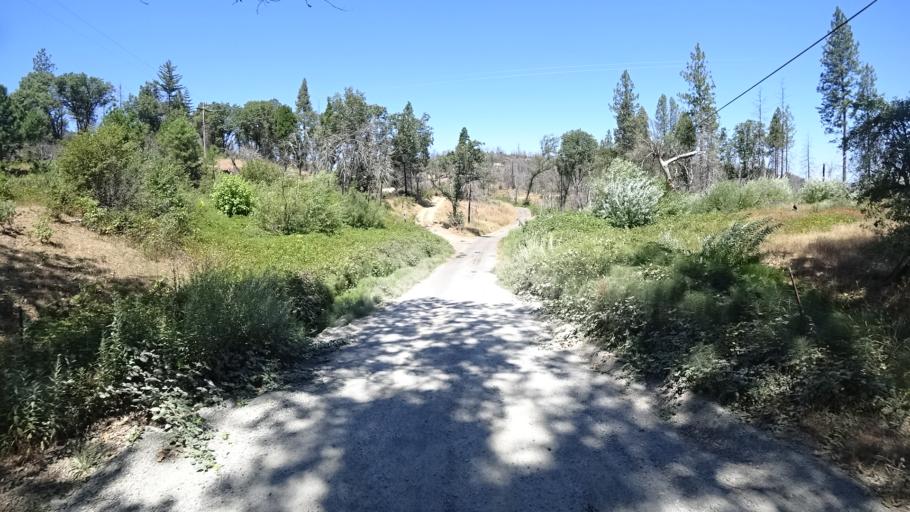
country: US
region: California
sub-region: Calaveras County
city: Mountain Ranch
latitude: 38.2343
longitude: -120.6033
